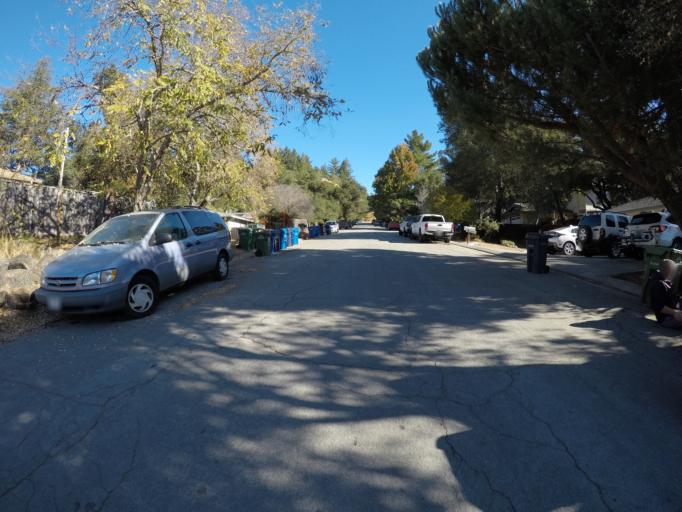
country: US
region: California
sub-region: Santa Cruz County
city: Scotts Valley
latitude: 37.0487
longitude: -122.0237
